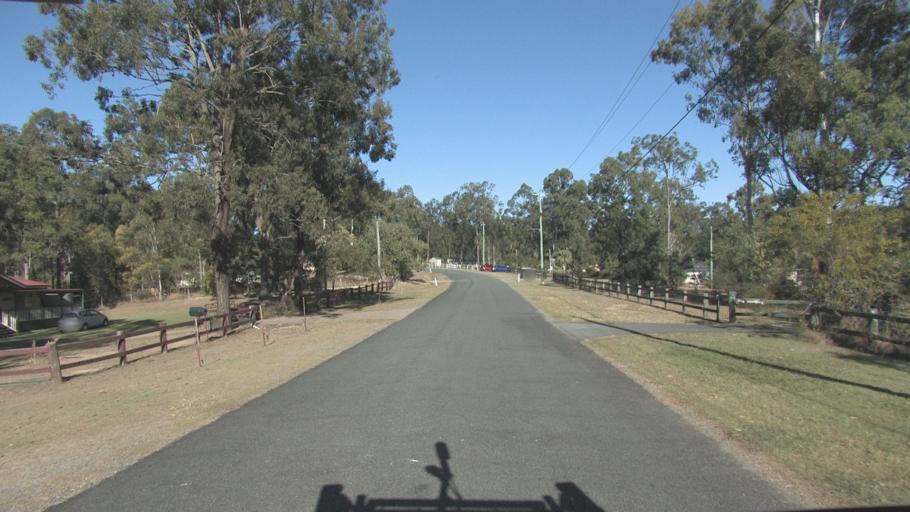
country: AU
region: Queensland
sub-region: Ipswich
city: Springfield Lakes
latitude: -27.6978
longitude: 152.9311
